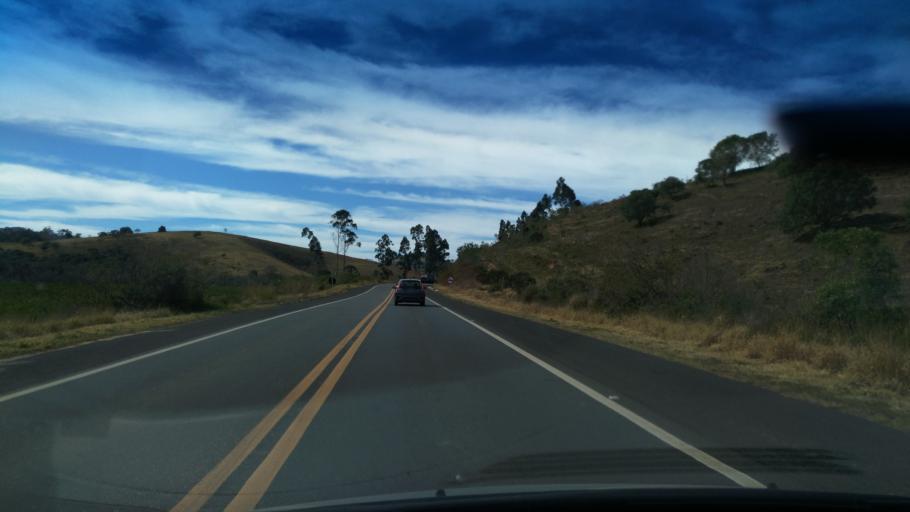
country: BR
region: Minas Gerais
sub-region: Borda Da Mata
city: Borda da Mata
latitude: -22.0742
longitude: -46.2617
